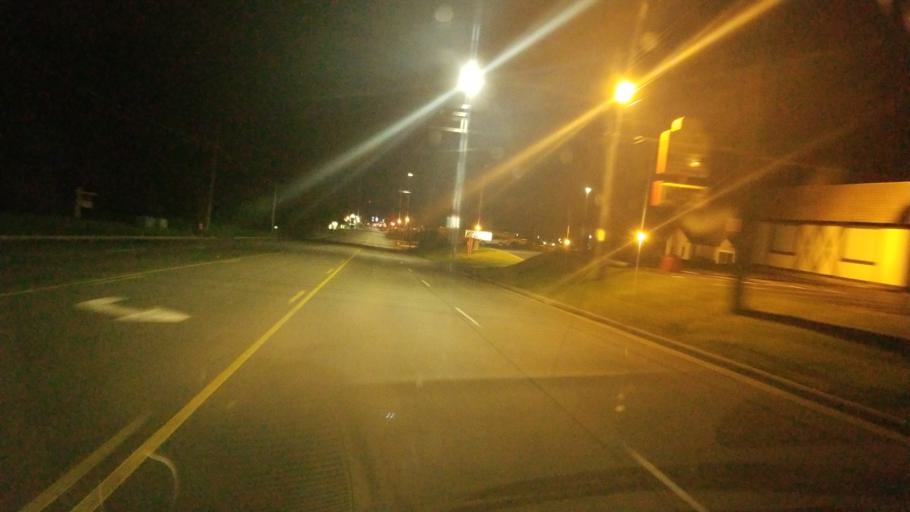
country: US
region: Ohio
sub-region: Trumbull County
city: McKinley Heights
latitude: 41.2013
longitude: -80.7344
